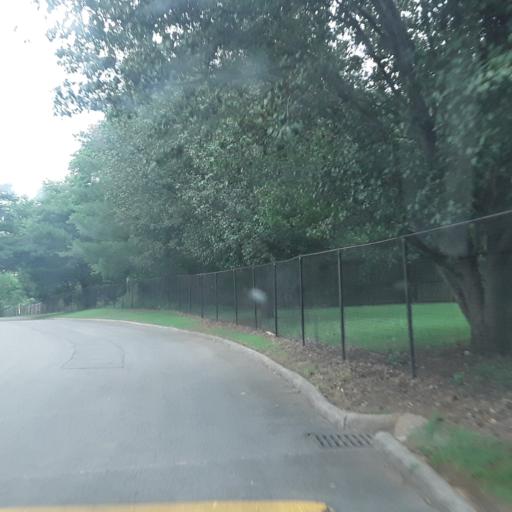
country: US
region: Tennessee
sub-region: Wilson County
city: Green Hill
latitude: 36.1625
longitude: -86.5935
